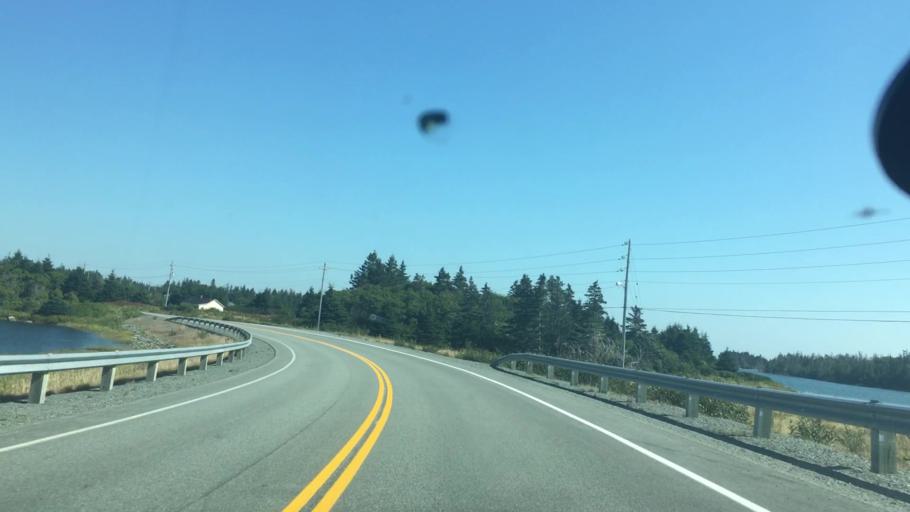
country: CA
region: Nova Scotia
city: New Glasgow
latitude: 44.9180
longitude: -62.3064
